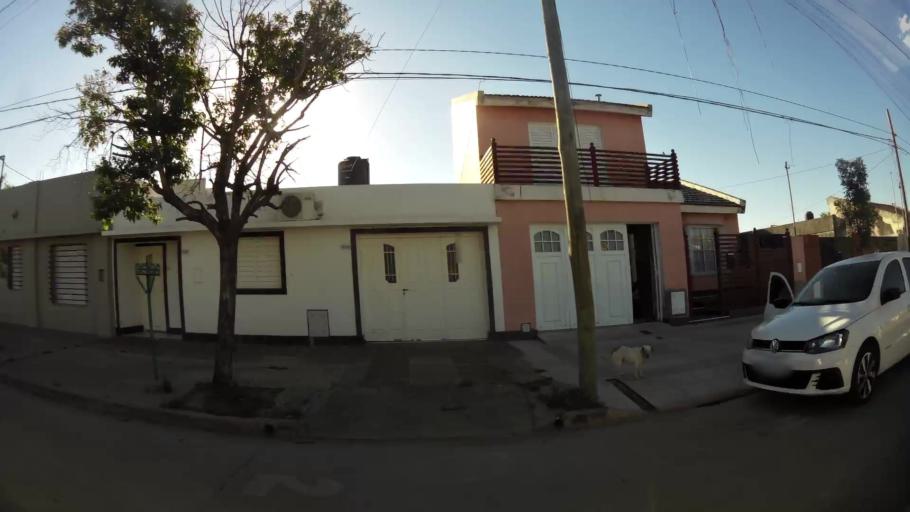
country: AR
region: Cordoba
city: San Francisco
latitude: -31.4429
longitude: -62.0950
